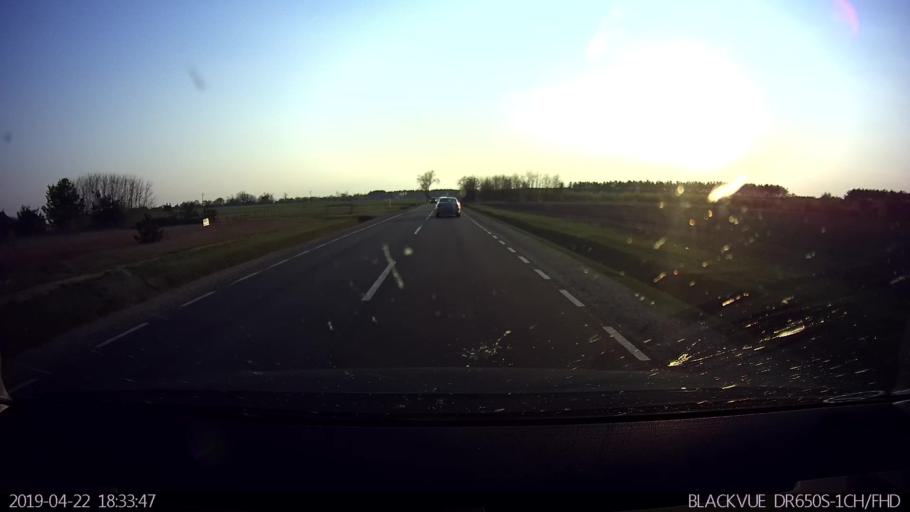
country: PL
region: Masovian Voivodeship
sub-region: Powiat wolominski
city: Jasienica
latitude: 52.4467
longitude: 21.3804
